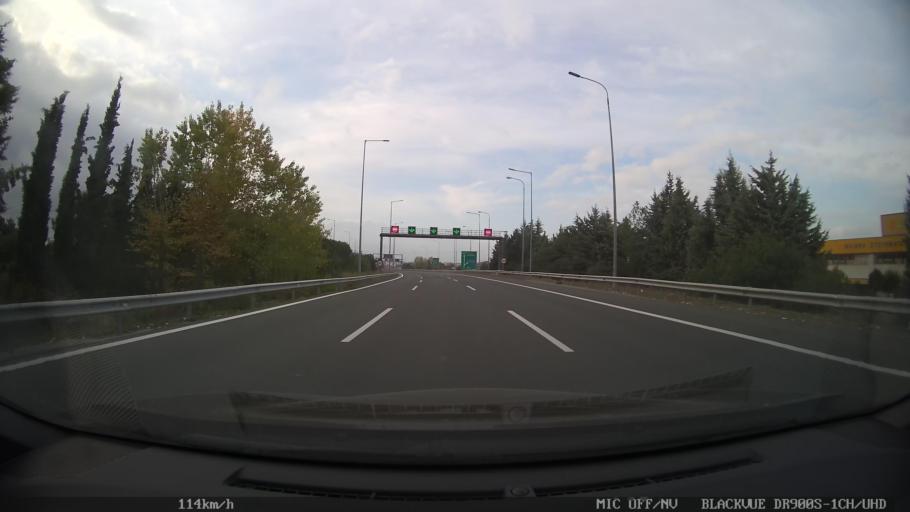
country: GR
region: Central Macedonia
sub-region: Nomos Pierias
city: Peristasi
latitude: 40.2824
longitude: 22.5247
